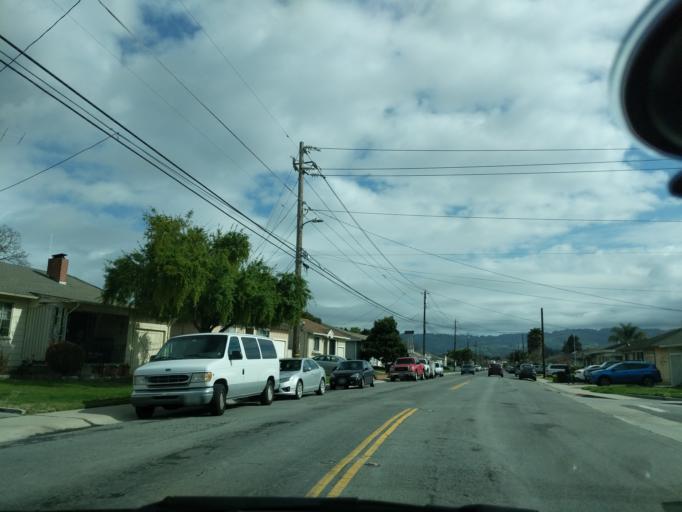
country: US
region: California
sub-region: Santa Cruz County
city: Freedom
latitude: 36.9266
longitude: -121.7716
